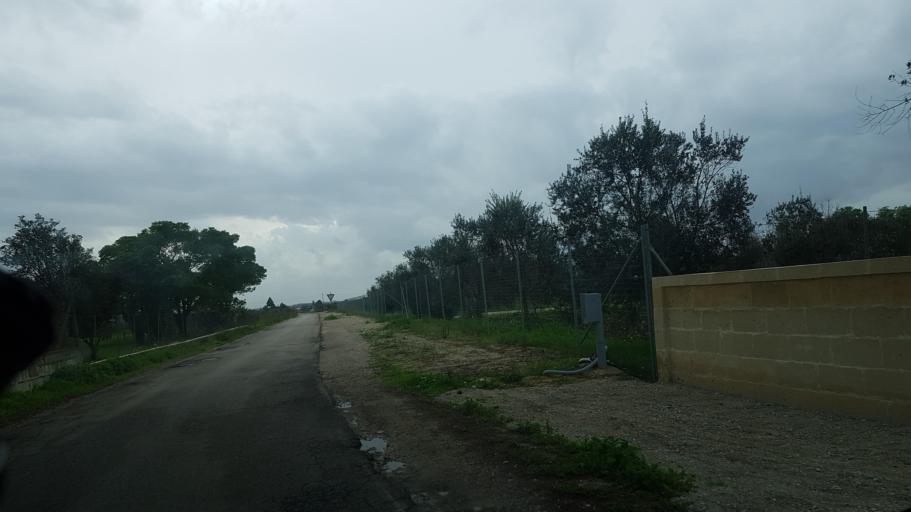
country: IT
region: Apulia
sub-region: Provincia di Lecce
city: Campi Salentina
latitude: 40.3858
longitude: 18.0222
